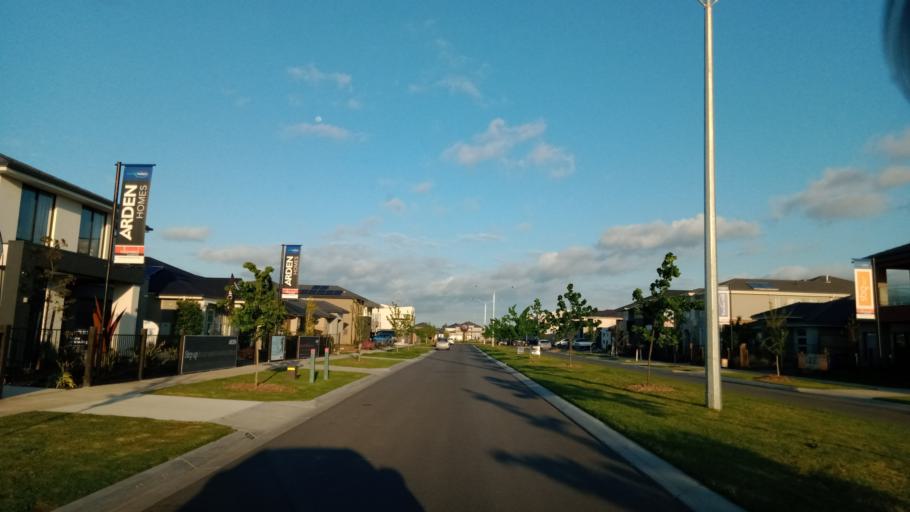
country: AU
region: Victoria
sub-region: Casey
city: Lynbrook
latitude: -38.0779
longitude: 145.2538
